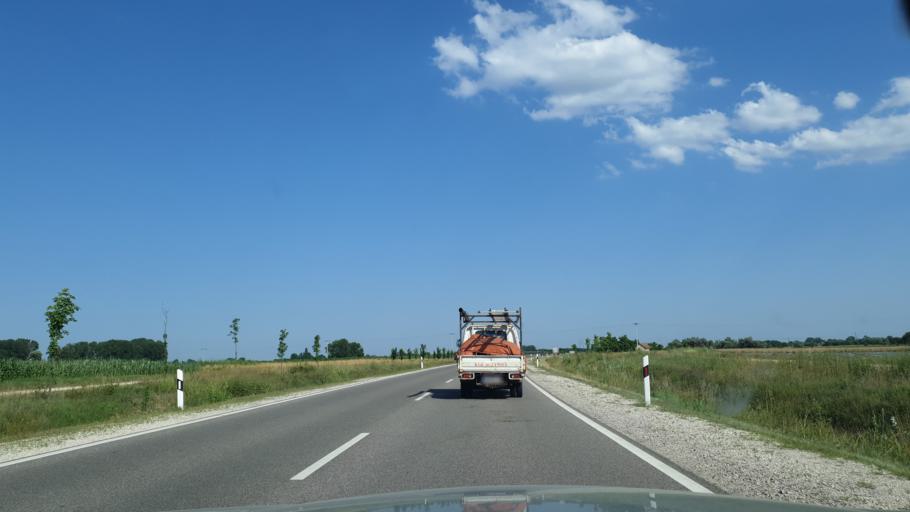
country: HU
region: Csongrad
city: Morahalom
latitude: 46.2359
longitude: 19.8846
